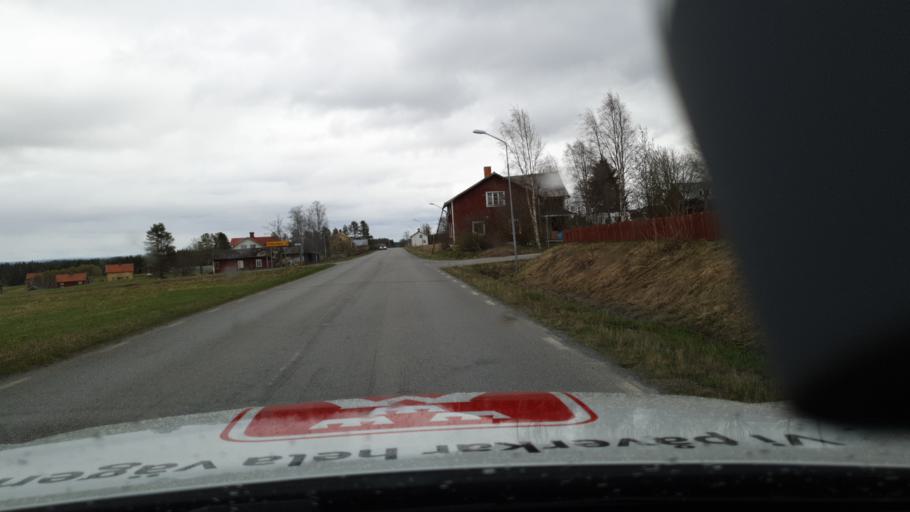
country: SE
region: Jaemtland
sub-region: Stroemsunds Kommun
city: Stroemsund
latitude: 63.6260
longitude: 15.2438
